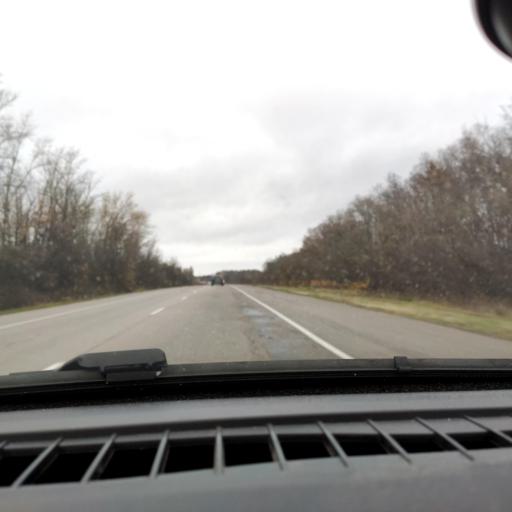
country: RU
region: Voronezj
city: Kolodeznyy
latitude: 51.2611
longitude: 39.0519
